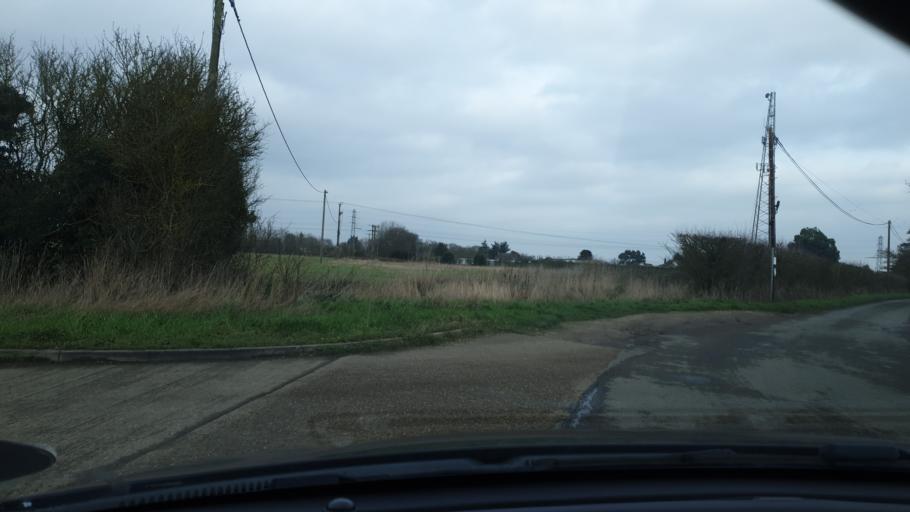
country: GB
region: England
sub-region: Essex
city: Alresford
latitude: 51.8600
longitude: 0.9925
